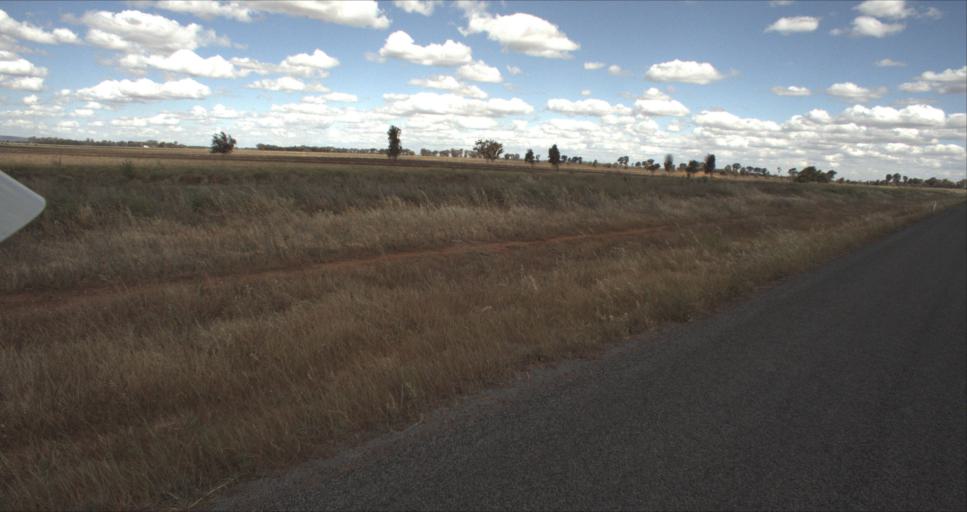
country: AU
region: New South Wales
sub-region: Leeton
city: Leeton
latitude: -34.4506
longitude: 146.2546
